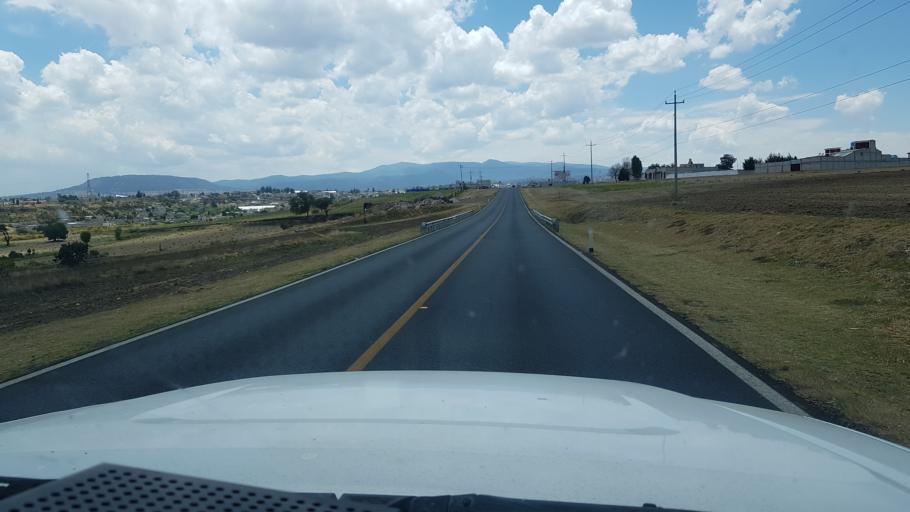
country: MX
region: Hidalgo
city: Calpulalpan
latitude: 19.6044
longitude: -98.5644
